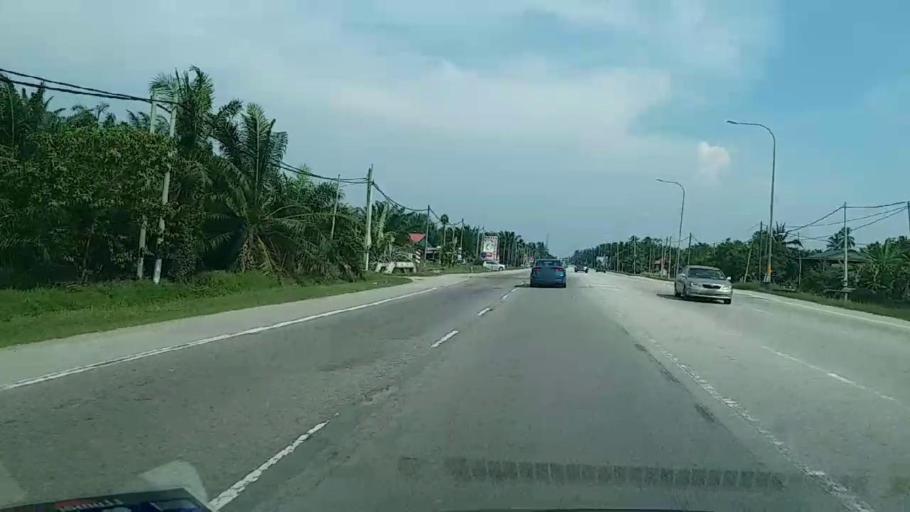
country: MY
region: Selangor
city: Kuala Selangor
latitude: 3.3736
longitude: 101.2390
